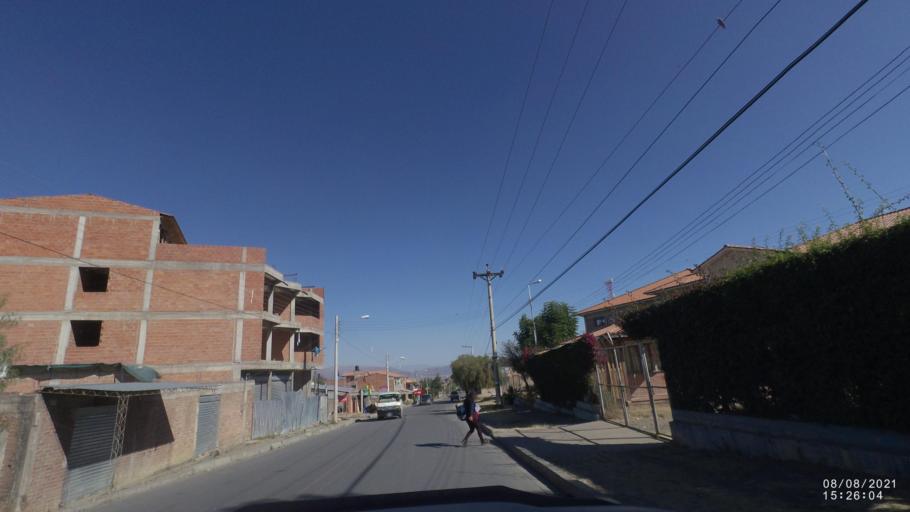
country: BO
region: Cochabamba
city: Cochabamba
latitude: -17.3205
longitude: -66.2815
